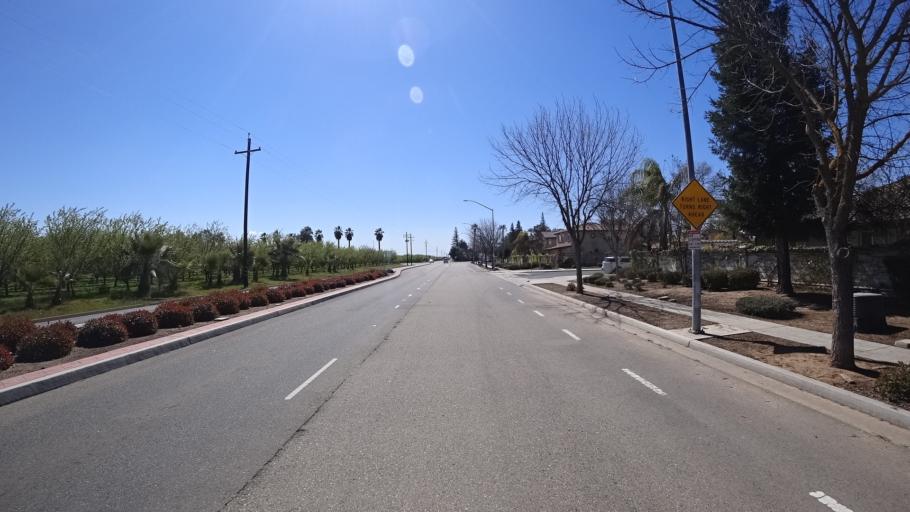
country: US
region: California
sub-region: Fresno County
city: West Park
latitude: 36.7299
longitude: -119.8446
